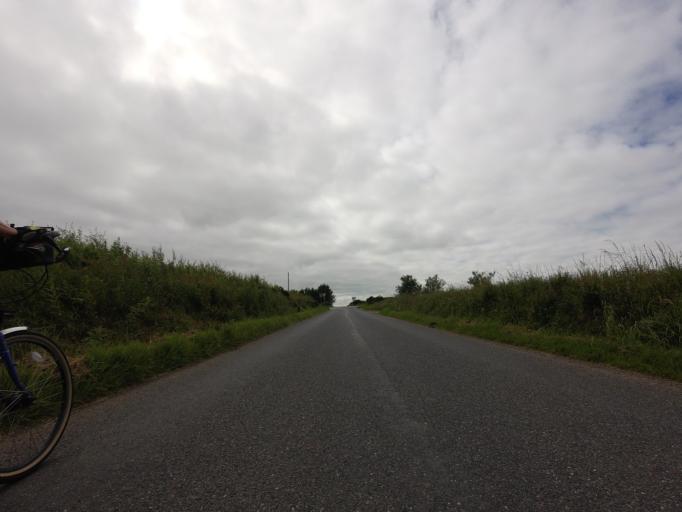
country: GB
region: Scotland
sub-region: Aberdeenshire
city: Rosehearty
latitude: 57.5437
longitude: -2.2429
